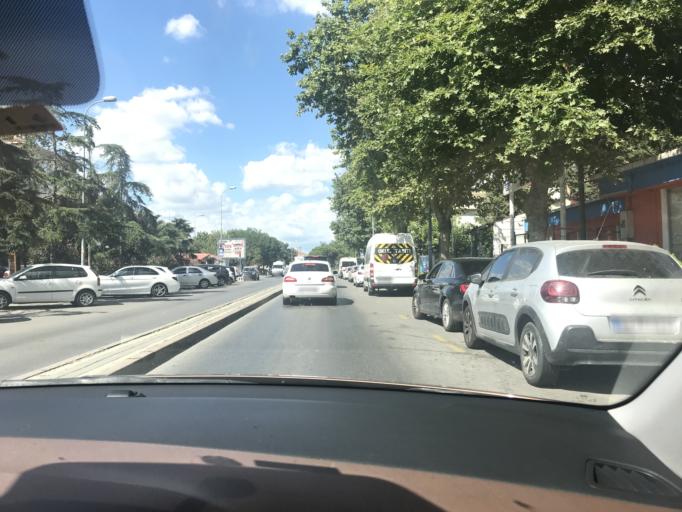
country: TR
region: Istanbul
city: UEskuedar
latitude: 41.0141
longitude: 29.0241
